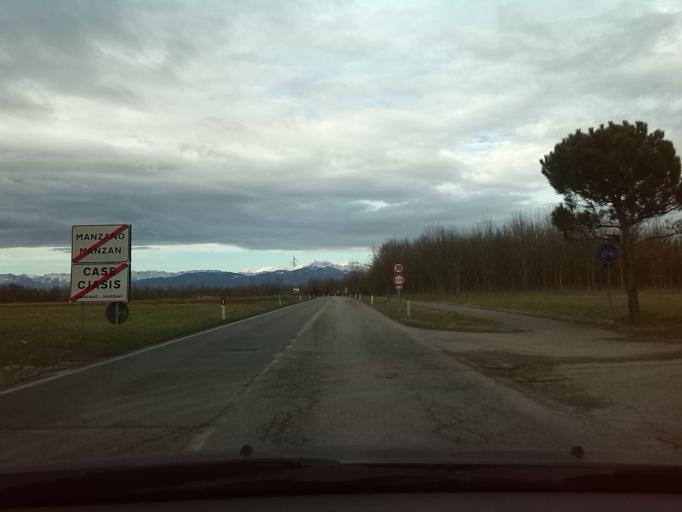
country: IT
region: Friuli Venezia Giulia
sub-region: Provincia di Udine
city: Manzano
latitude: 45.9998
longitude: 13.3916
